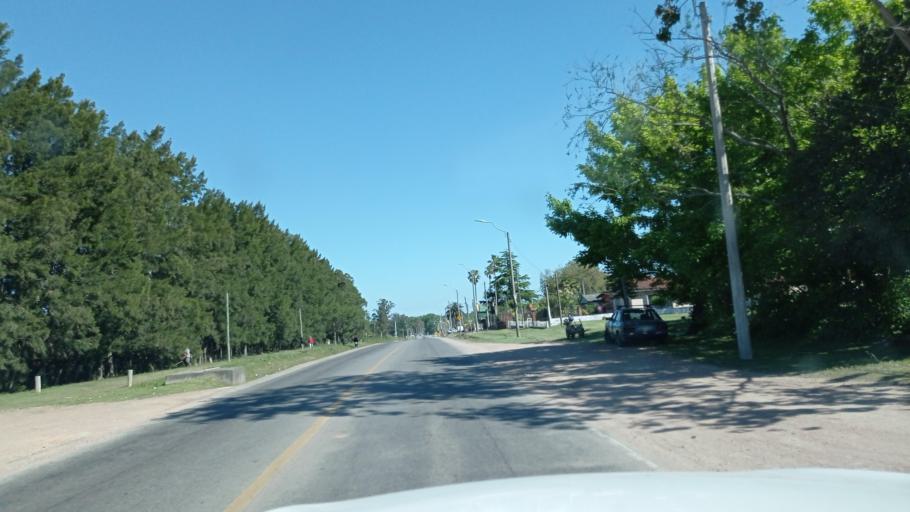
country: UY
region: Canelones
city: La Paz
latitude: -34.7905
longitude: -56.1656
